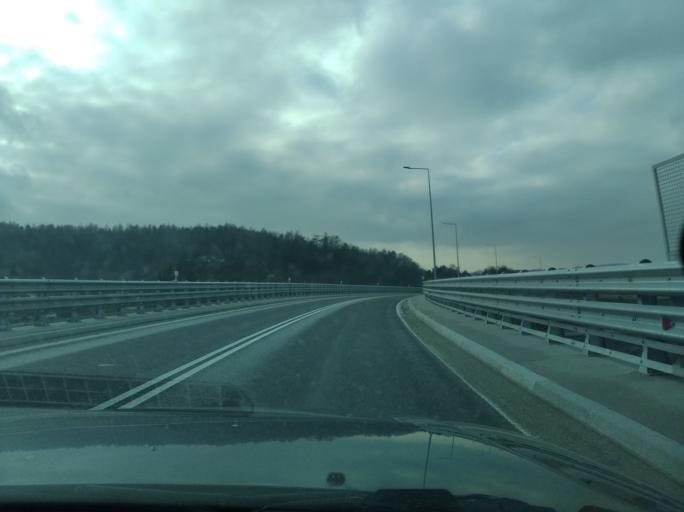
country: PL
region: Subcarpathian Voivodeship
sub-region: Powiat strzyzowski
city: Czudec
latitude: 49.9420
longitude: 21.8480
